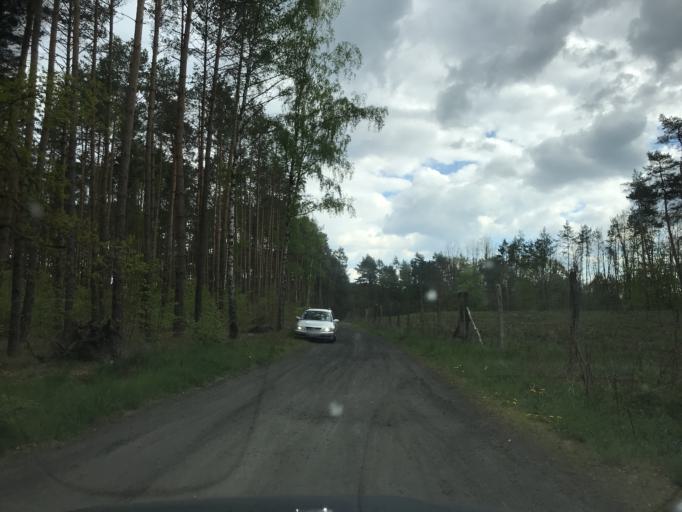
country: PL
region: West Pomeranian Voivodeship
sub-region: Powiat mysliborski
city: Mysliborz
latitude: 52.8632
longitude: 14.8864
